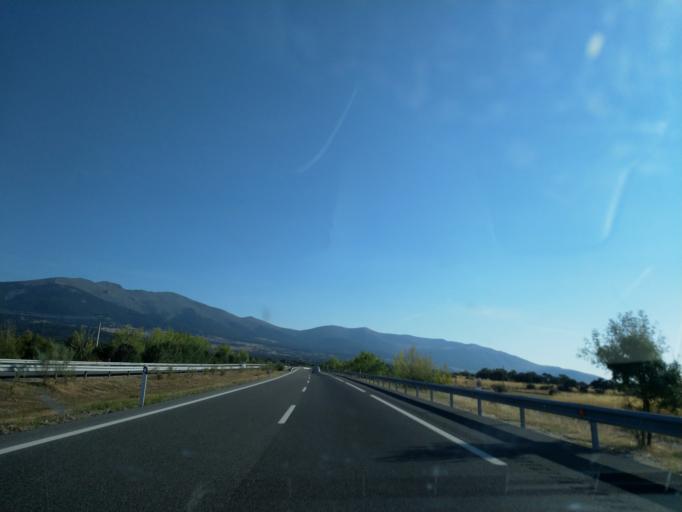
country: ES
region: Castille and Leon
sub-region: Provincia de Segovia
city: Segovia
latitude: 40.8860
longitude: -4.1169
